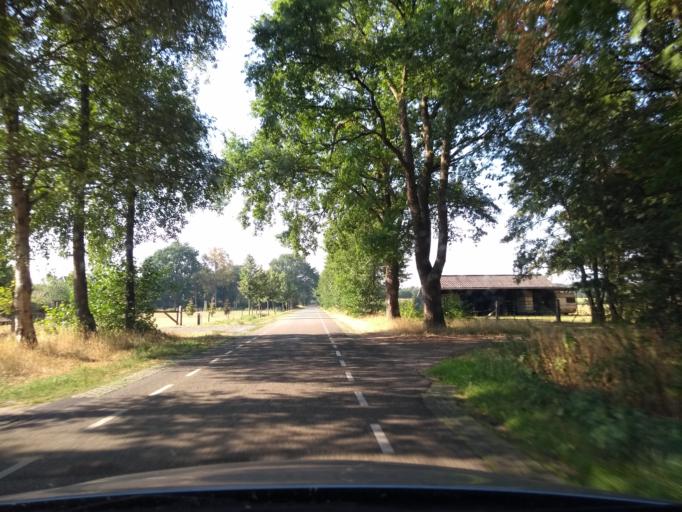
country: NL
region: Overijssel
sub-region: Gemeente Haaksbergen
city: Haaksbergen
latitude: 52.1397
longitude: 6.7466
